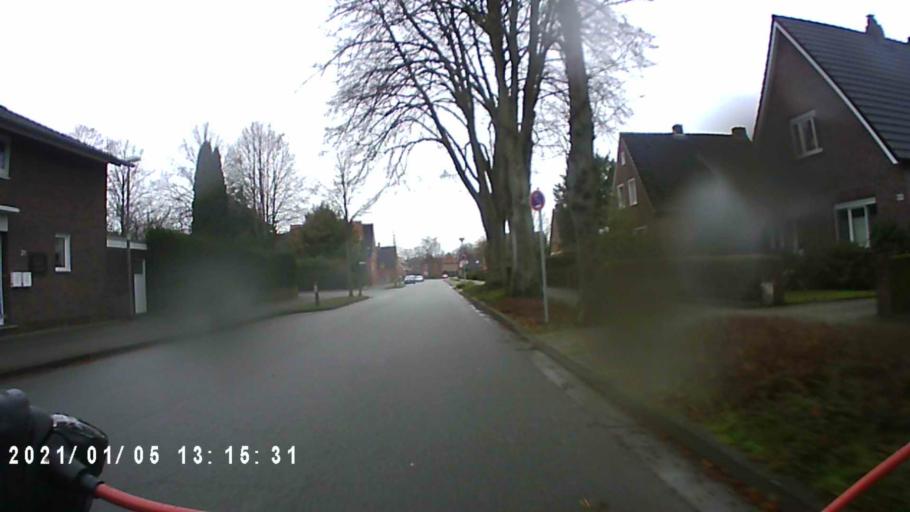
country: DE
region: Lower Saxony
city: Leer
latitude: 53.2380
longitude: 7.4510
